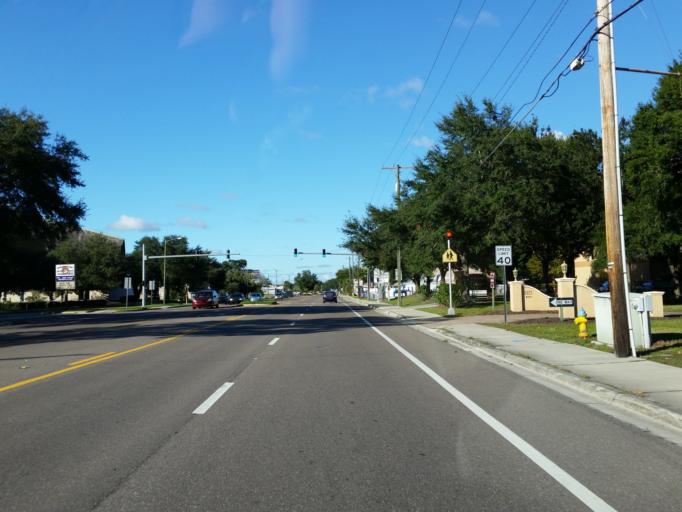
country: US
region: Florida
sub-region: Hillsborough County
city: Tampa
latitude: 27.8988
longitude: -82.5183
